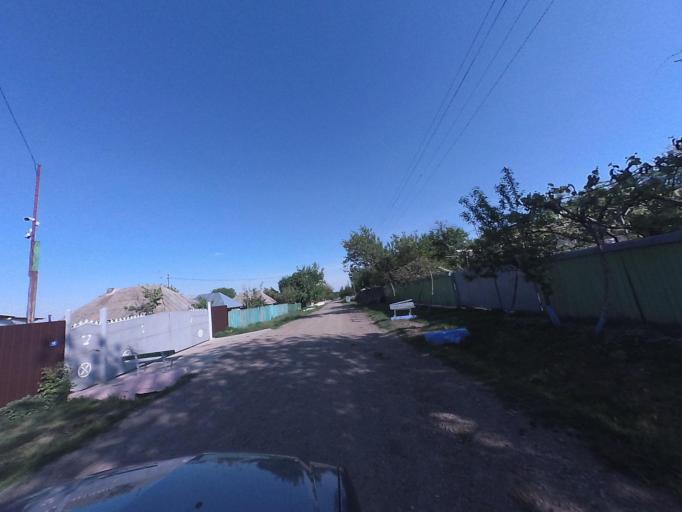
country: RO
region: Neamt
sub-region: Comuna Dulcesti
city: Dulcesti
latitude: 47.0035
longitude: 26.7733
